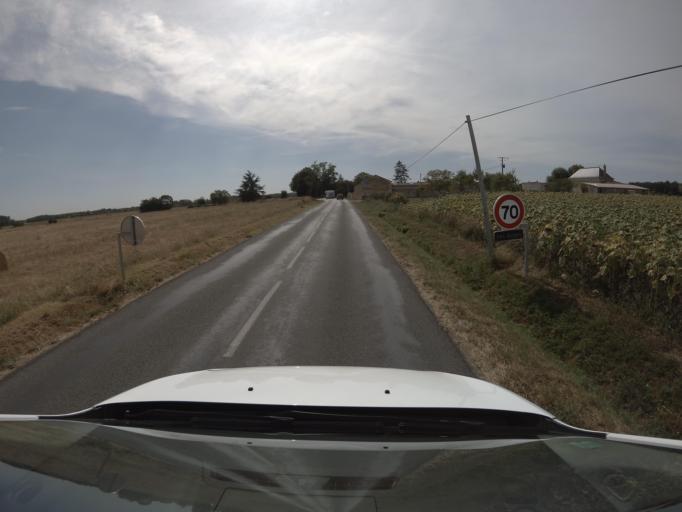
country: FR
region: Poitou-Charentes
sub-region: Departement des Deux-Sevres
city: Saint-Leger-de-Montbrun
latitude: 47.0054
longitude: -0.0841
